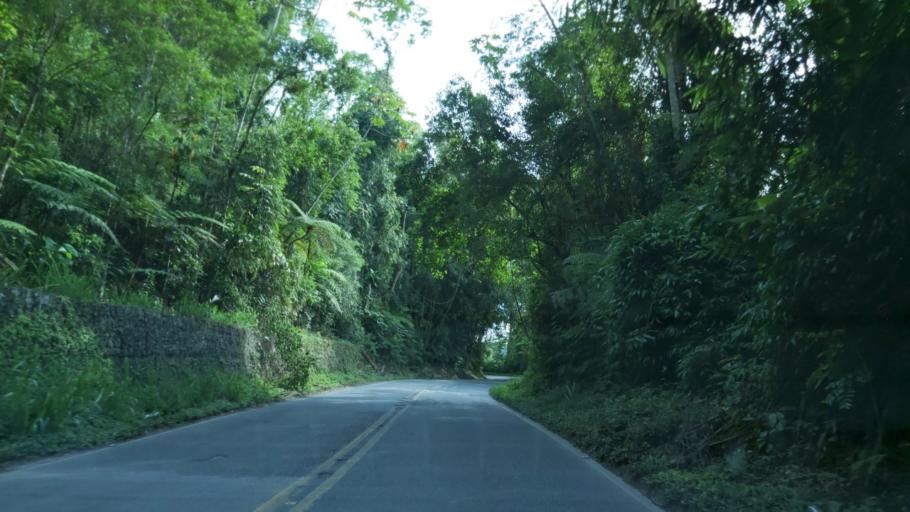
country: BR
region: Sao Paulo
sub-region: Juquia
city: Juquia
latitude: -24.0973
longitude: -47.6162
